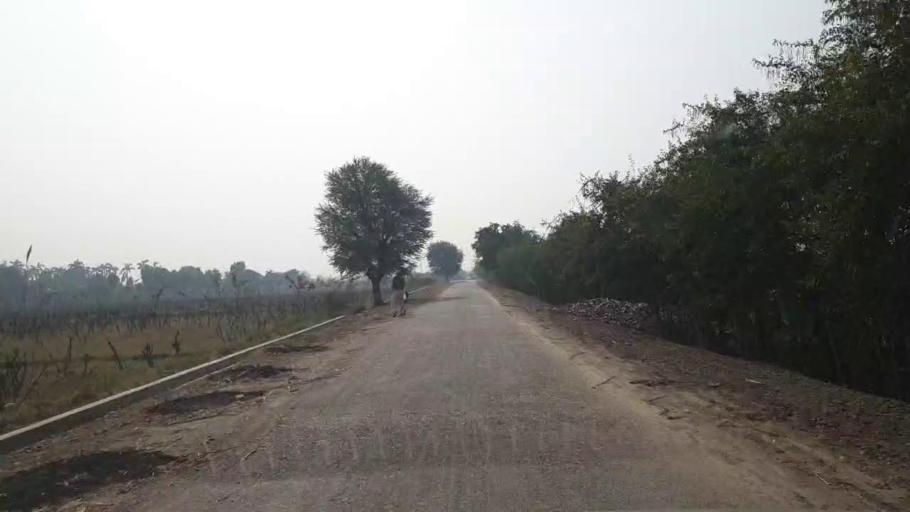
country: PK
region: Sindh
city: Hala
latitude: 25.8245
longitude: 68.4377
